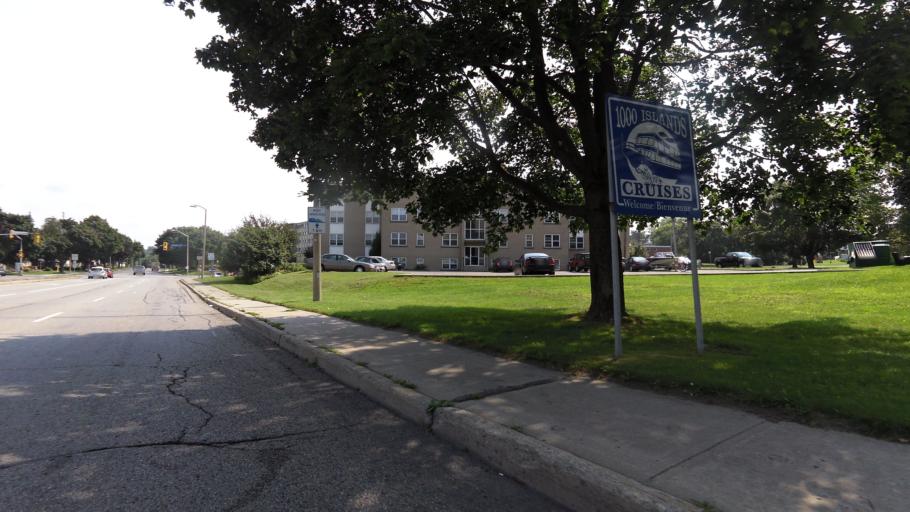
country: CA
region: Ontario
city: Brockville
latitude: 44.5982
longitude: -75.6978
